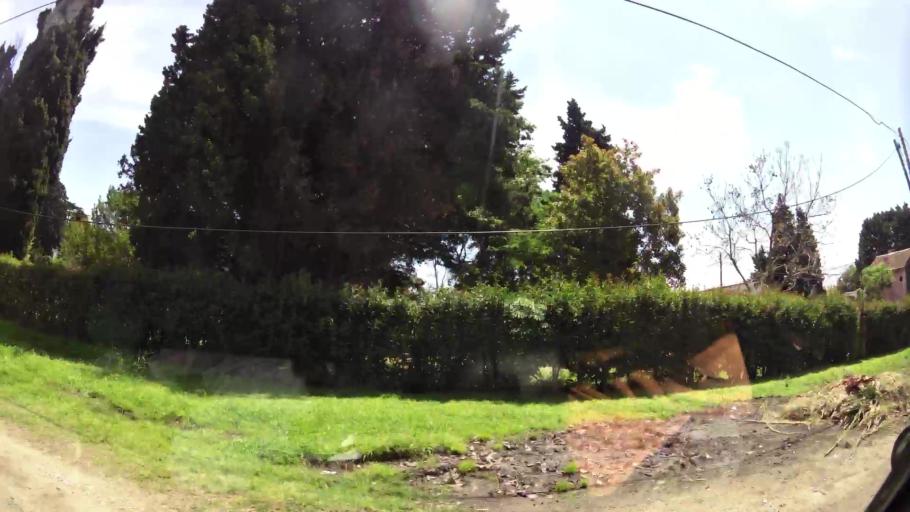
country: AR
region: Buenos Aires
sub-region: Partido de Quilmes
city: Quilmes
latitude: -34.7861
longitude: -58.2695
